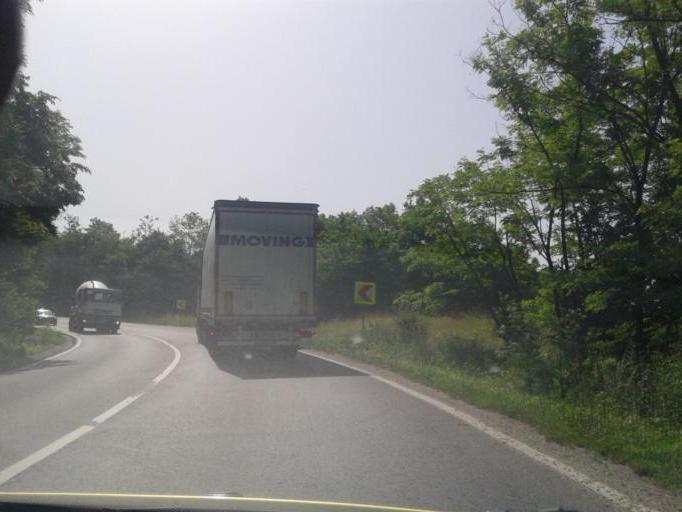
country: RO
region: Arges
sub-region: Comuna Moraresti
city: Moraresti
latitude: 45.0045
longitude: 24.5543
